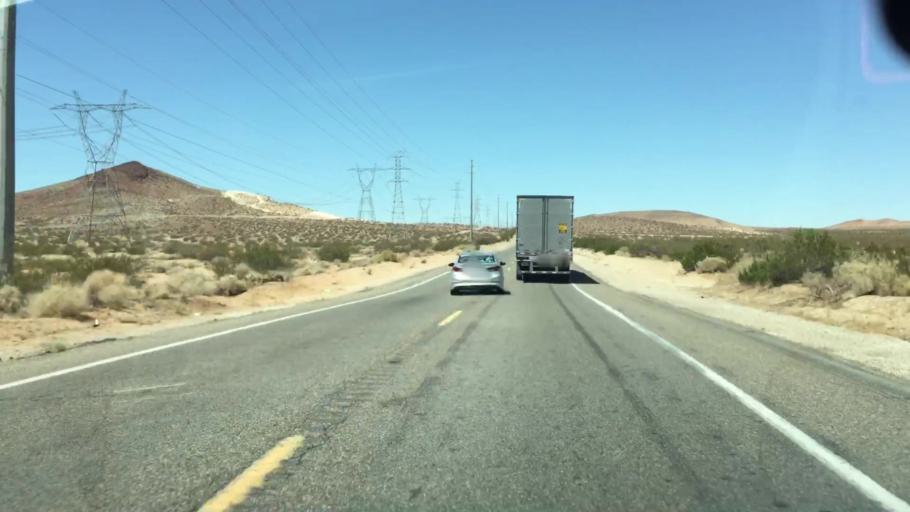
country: US
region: California
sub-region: Kern County
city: Boron
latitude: 34.8590
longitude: -117.5046
